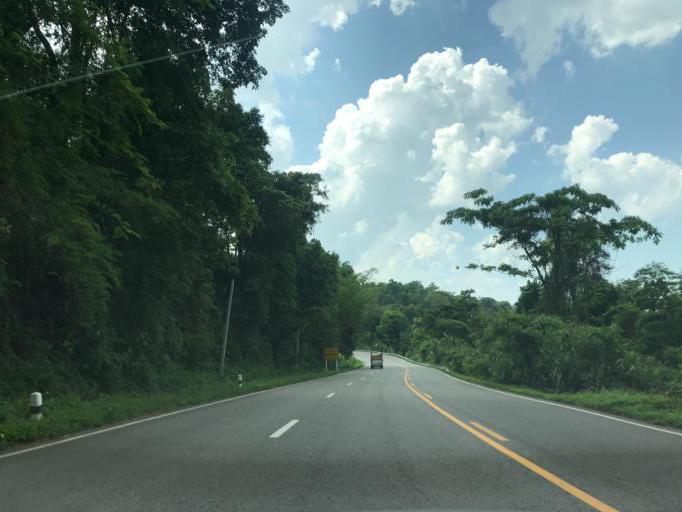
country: TH
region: Phayao
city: Phayao
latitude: 19.0660
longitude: 99.8045
